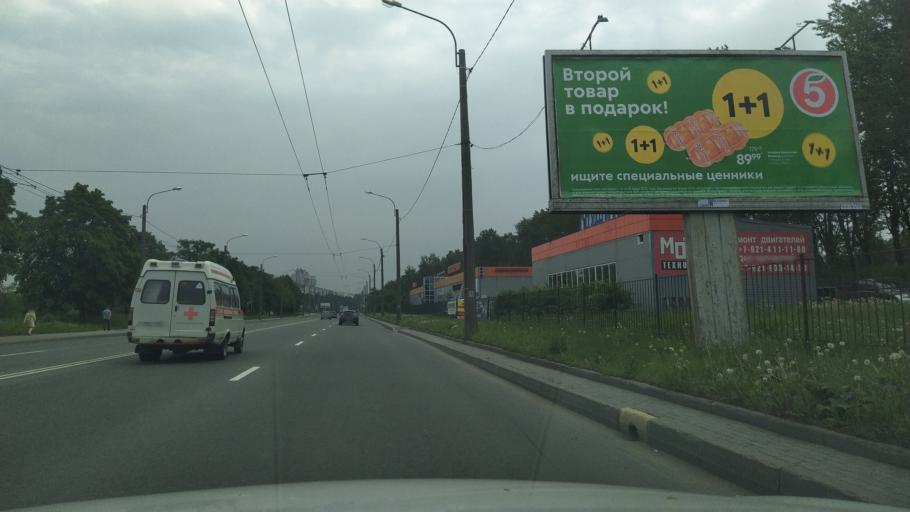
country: RU
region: St.-Petersburg
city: Kupchino
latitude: 59.8770
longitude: 30.3535
